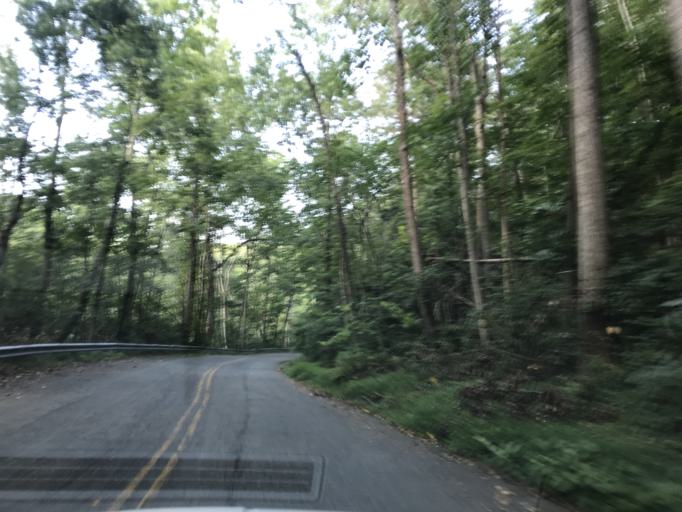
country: US
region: Maryland
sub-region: Harford County
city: South Bel Air
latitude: 39.6121
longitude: -76.2884
